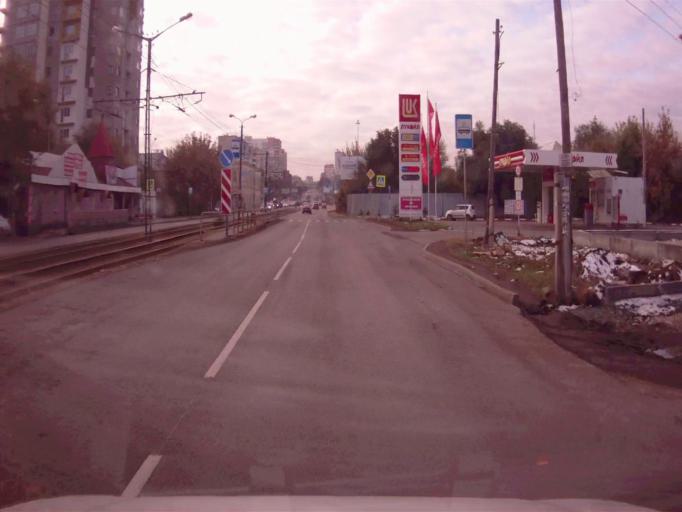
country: RU
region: Chelyabinsk
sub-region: Gorod Chelyabinsk
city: Chelyabinsk
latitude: 55.1703
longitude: 61.4154
